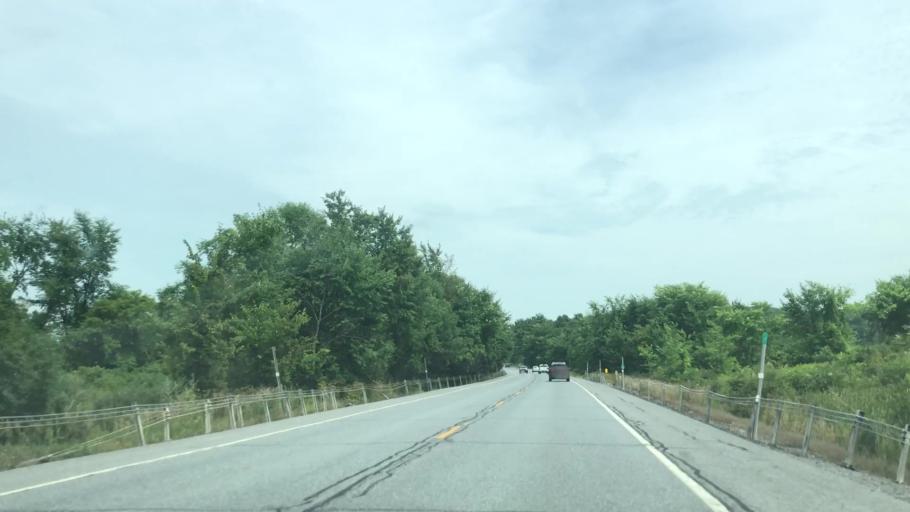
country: US
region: New York
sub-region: Washington County
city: Whitehall
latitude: 43.5501
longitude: -73.3692
